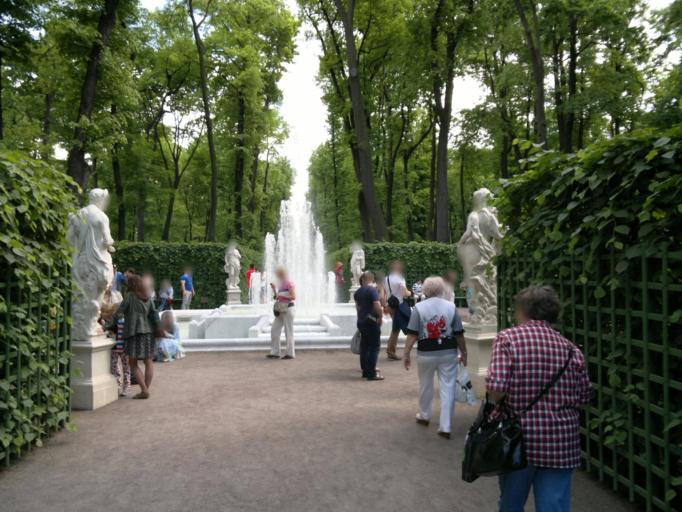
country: RU
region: St.-Petersburg
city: Saint Petersburg
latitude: 59.9457
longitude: 30.3350
